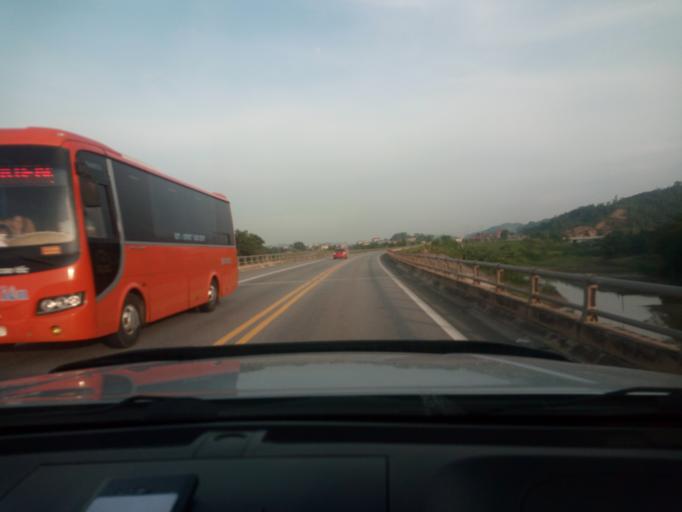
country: VN
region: Yen Bai
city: Co Phuc
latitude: 21.8842
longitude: 104.6676
